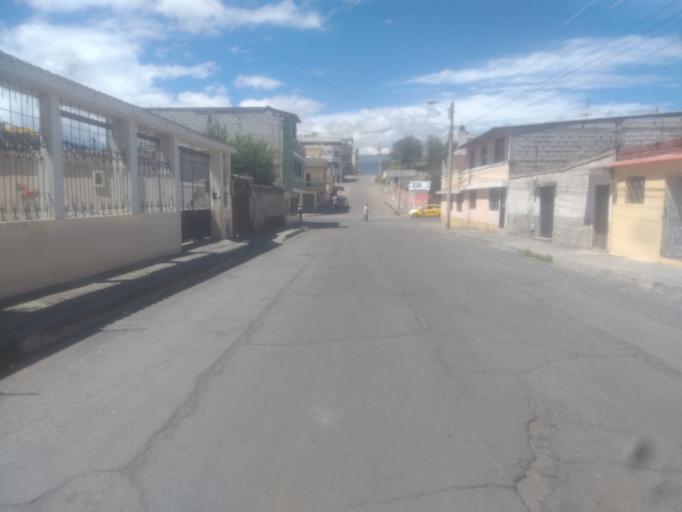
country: EC
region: Chimborazo
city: Riobamba
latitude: -1.6625
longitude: -78.6467
